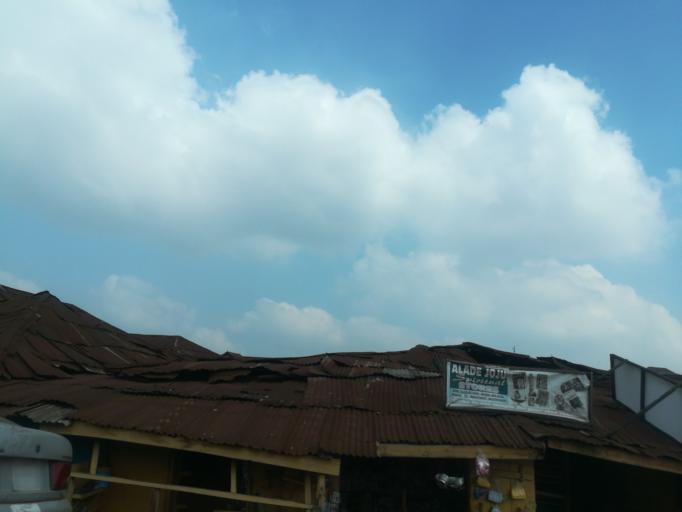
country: NG
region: Oyo
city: Ibadan
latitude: 7.3791
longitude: 3.8971
